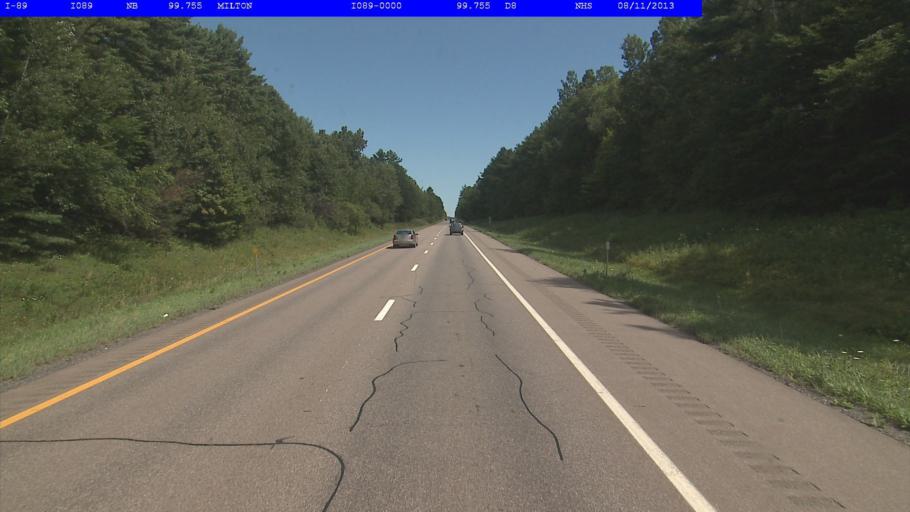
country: US
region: Vermont
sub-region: Chittenden County
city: Milton
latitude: 44.6148
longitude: -73.1615
